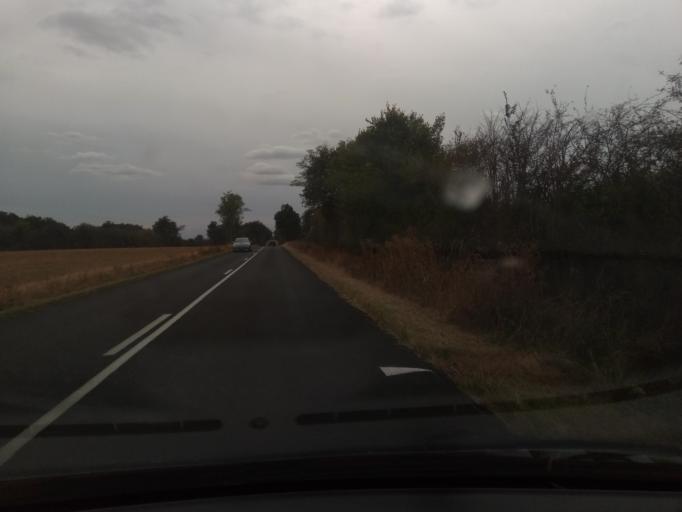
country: FR
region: Poitou-Charentes
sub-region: Departement de la Vienne
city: Pleumartin
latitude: 46.6488
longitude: 0.7666
